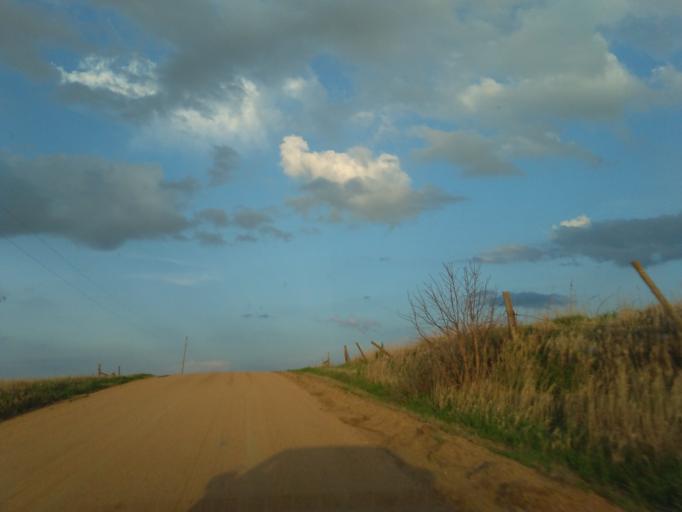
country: US
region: Nebraska
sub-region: Nuckolls County
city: Nelson
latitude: 40.2054
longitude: -98.2976
